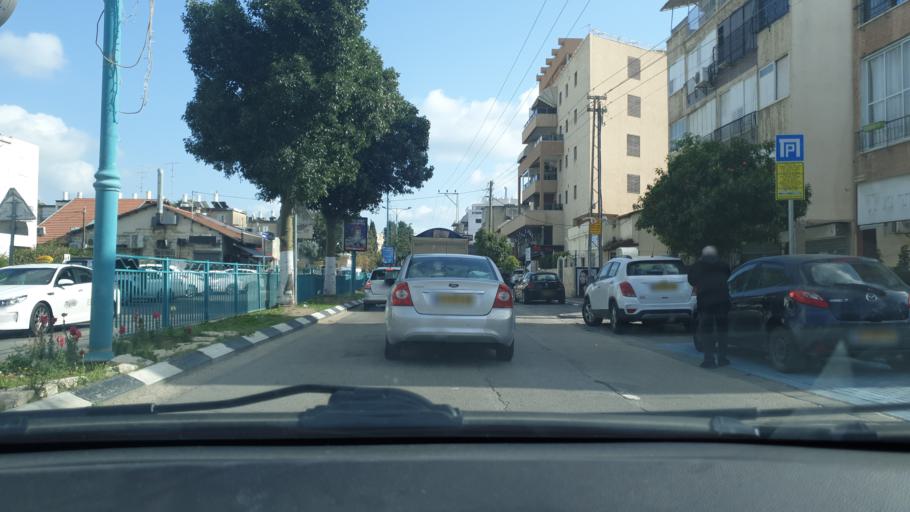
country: IL
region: Central District
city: Ramla
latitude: 31.9348
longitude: 34.8673
